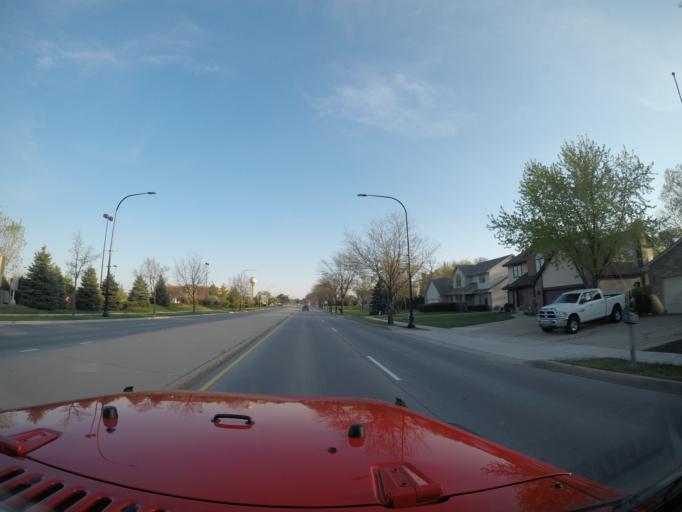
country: US
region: Illinois
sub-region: Cook County
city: Prospect Heights
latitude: 42.0851
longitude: -87.9369
